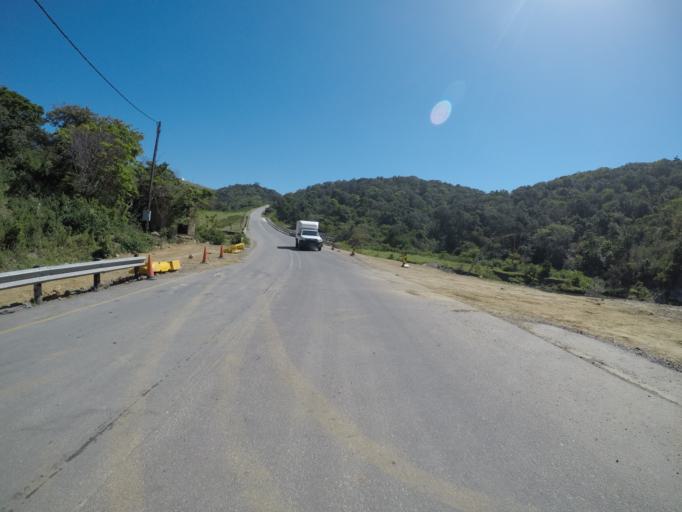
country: ZA
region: Eastern Cape
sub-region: OR Tambo District Municipality
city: Libode
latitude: -31.9779
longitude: 29.1484
